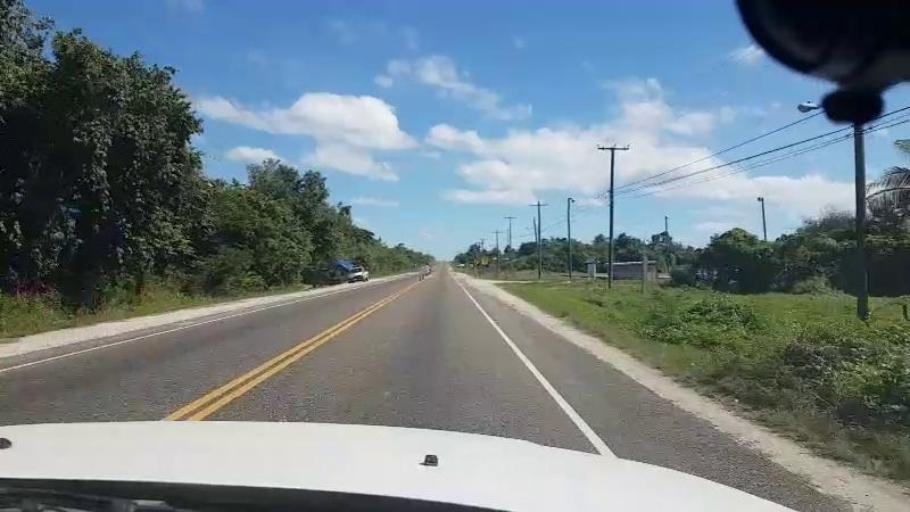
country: BZ
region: Cayo
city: Belmopan
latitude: 17.2769
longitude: -88.7120
